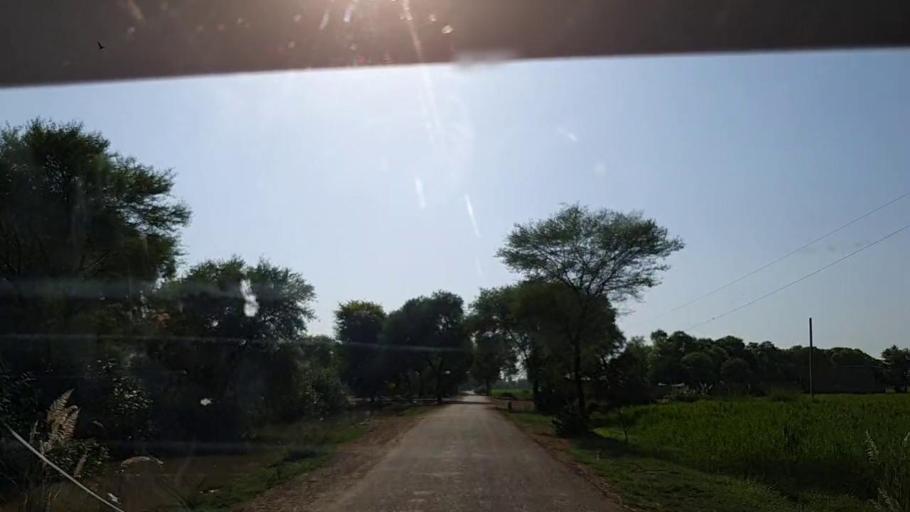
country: PK
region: Sindh
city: Tangwani
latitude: 28.2154
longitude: 68.9838
